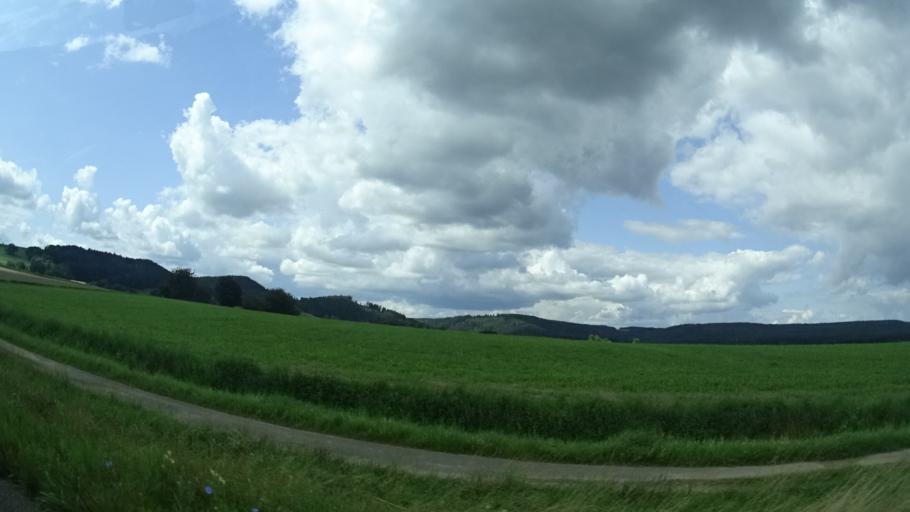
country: DE
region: Bavaria
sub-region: Upper Franconia
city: Neustadt bei Coburg
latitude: 50.2987
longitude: 11.1023
